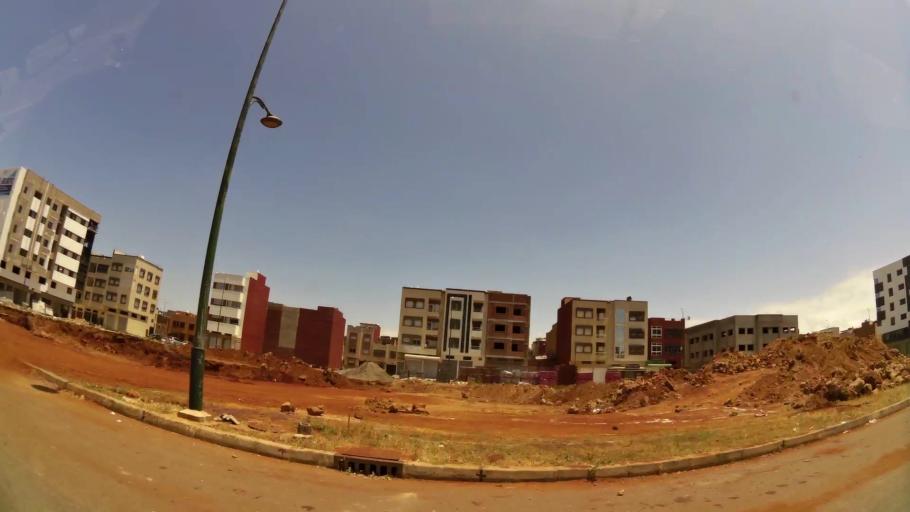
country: MA
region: Gharb-Chrarda-Beni Hssen
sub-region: Kenitra Province
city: Kenitra
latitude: 34.2682
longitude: -6.6271
